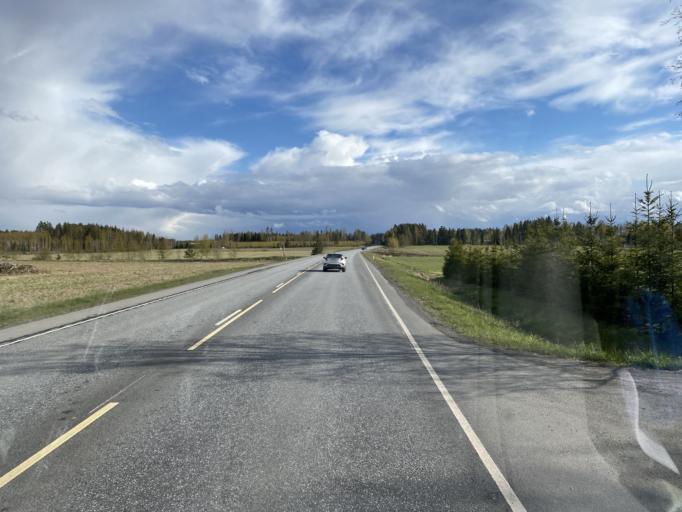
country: FI
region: Pirkanmaa
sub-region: Tampere
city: Lempaeaelae
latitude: 61.2904
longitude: 23.7425
